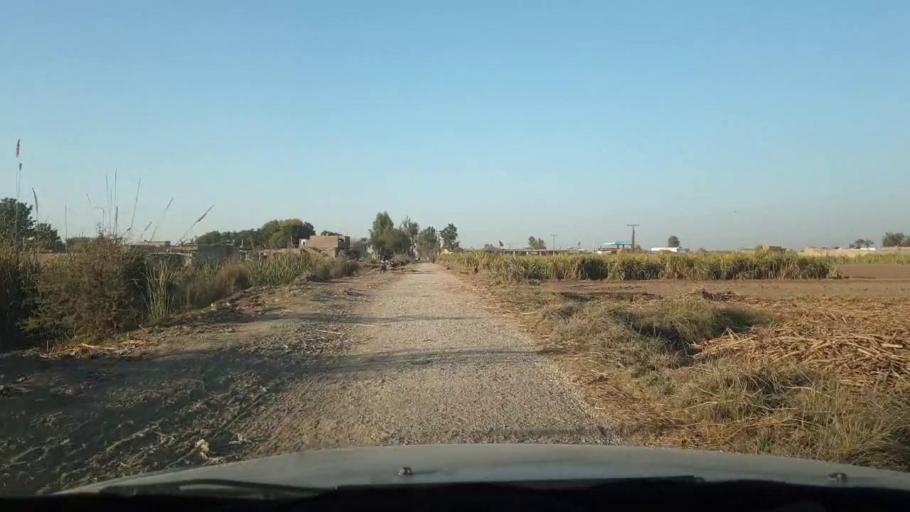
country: PK
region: Sindh
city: Ghotki
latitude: 27.9922
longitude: 69.2725
